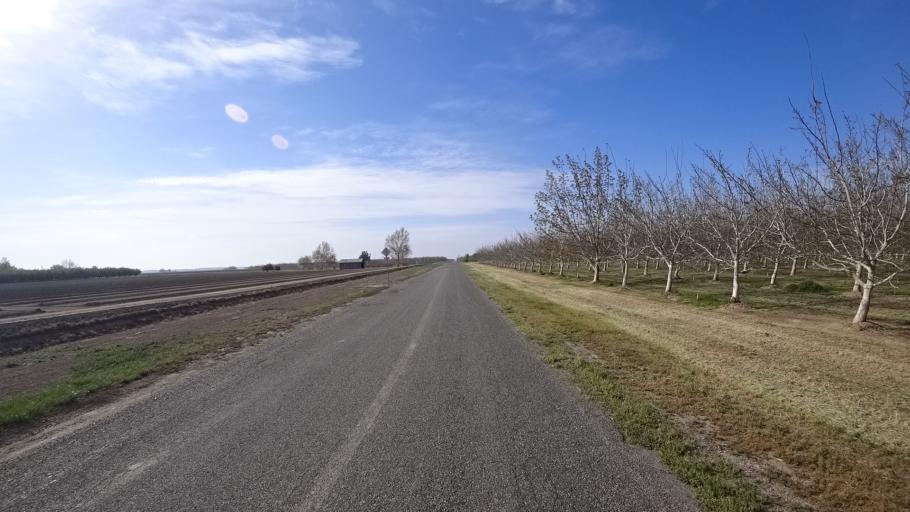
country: US
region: California
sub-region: Glenn County
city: Hamilton City
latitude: 39.6291
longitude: -122.0463
